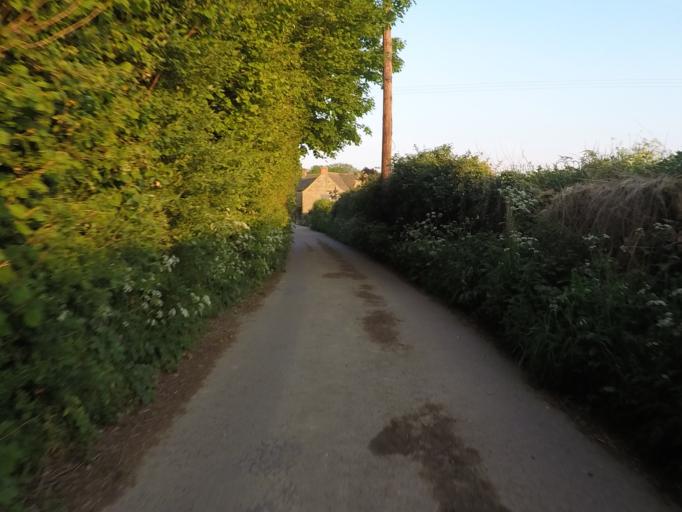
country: GB
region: England
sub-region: Oxfordshire
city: Charlbury
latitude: 51.8348
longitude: -1.5279
